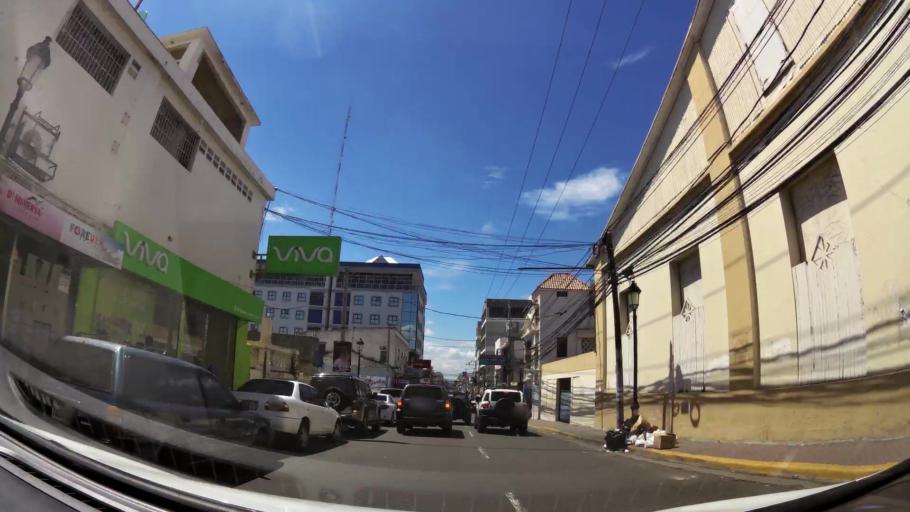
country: DO
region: Santiago
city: Santiago de los Caballeros
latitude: 19.4521
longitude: -70.6991
